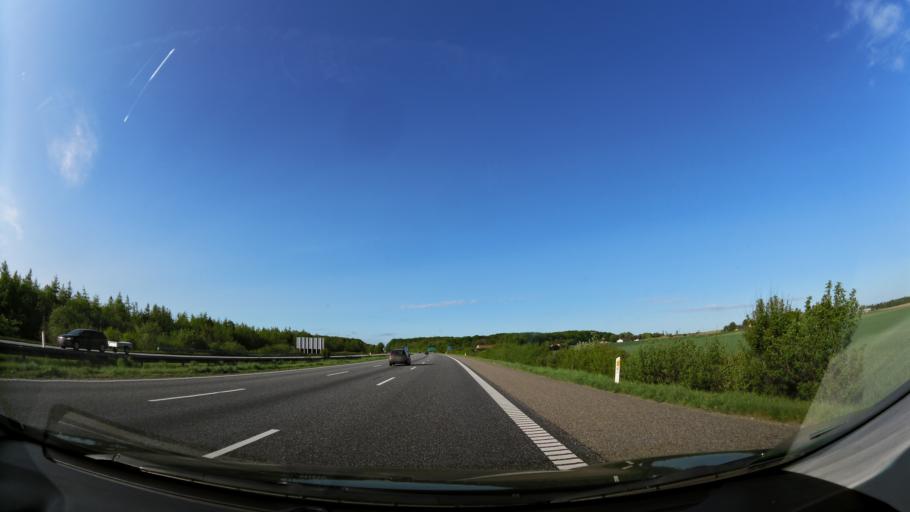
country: DK
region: Central Jutland
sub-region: Skanderborg Kommune
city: Horning
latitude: 56.0933
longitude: 10.0211
